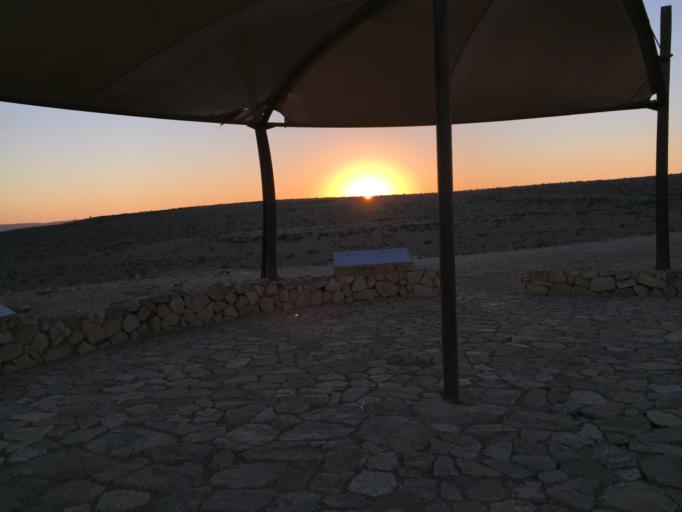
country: IL
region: Southern District
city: Midreshet Ben-Gurion
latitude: 30.8877
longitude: 34.7920
